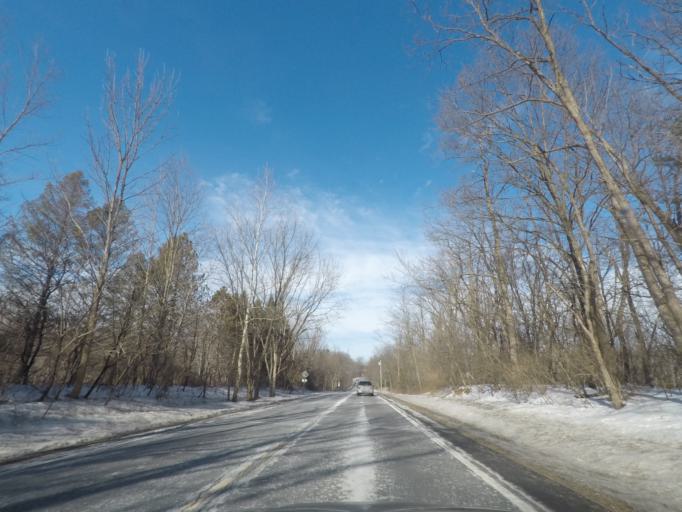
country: US
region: New York
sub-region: Albany County
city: Altamont
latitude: 42.7195
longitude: -73.9934
